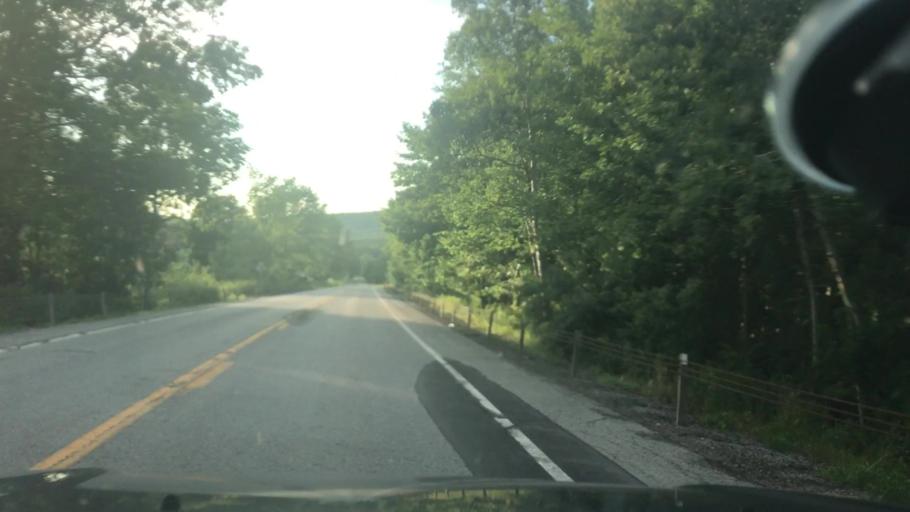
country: US
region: New York
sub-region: Otsego County
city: Unadilla
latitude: 42.3293
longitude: -75.2326
